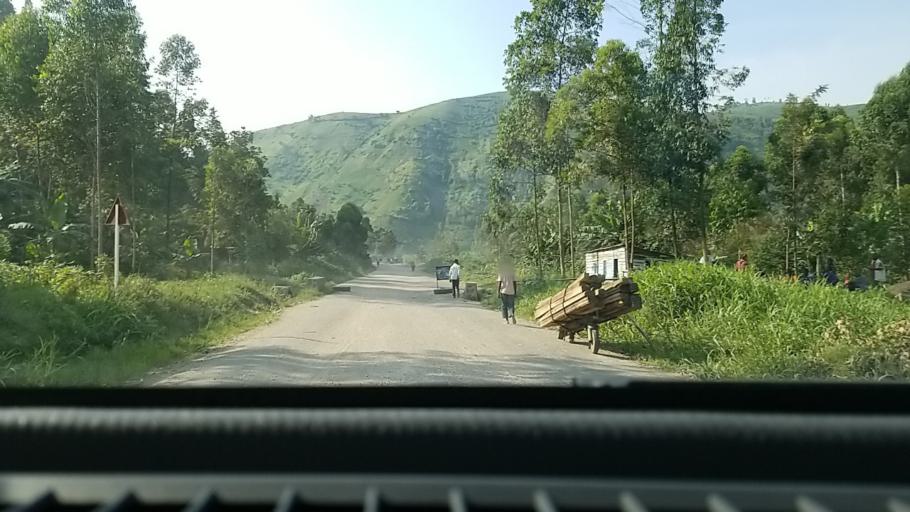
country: CD
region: Nord Kivu
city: Sake
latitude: -1.5679
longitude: 29.0436
